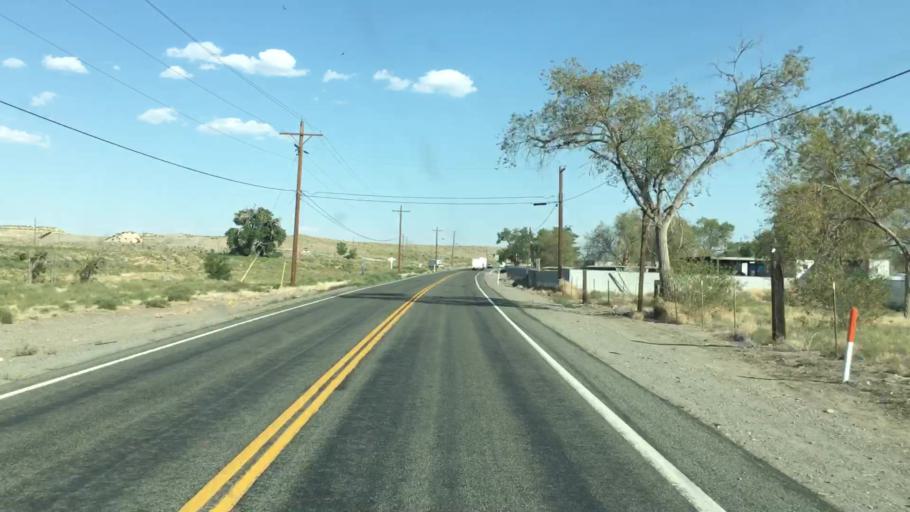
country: US
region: Nevada
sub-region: Lyon County
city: Fernley
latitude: 39.6313
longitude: -119.2806
